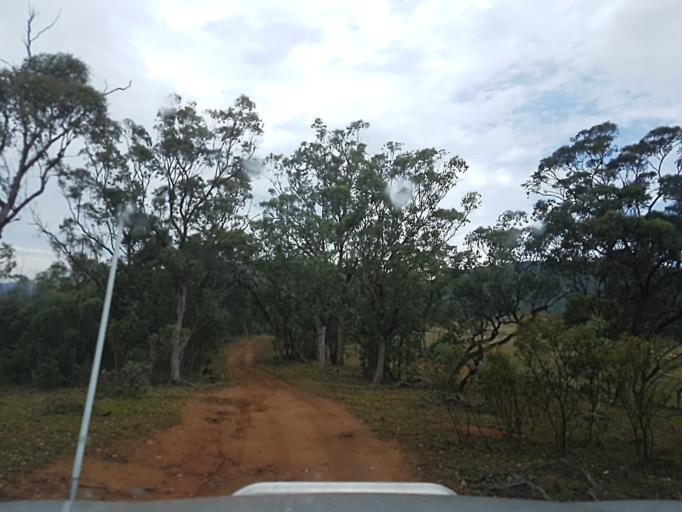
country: AU
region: New South Wales
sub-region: Snowy River
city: Jindabyne
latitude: -36.9631
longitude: 148.3814
